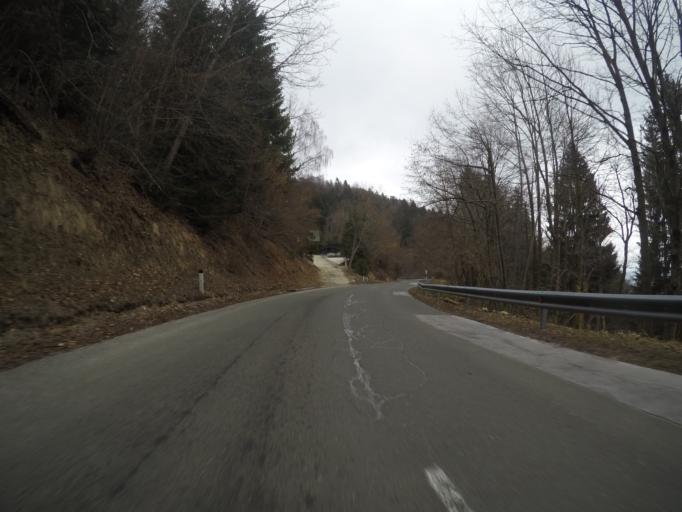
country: SI
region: Ruse
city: Ruse
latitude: 46.4987
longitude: 15.5533
